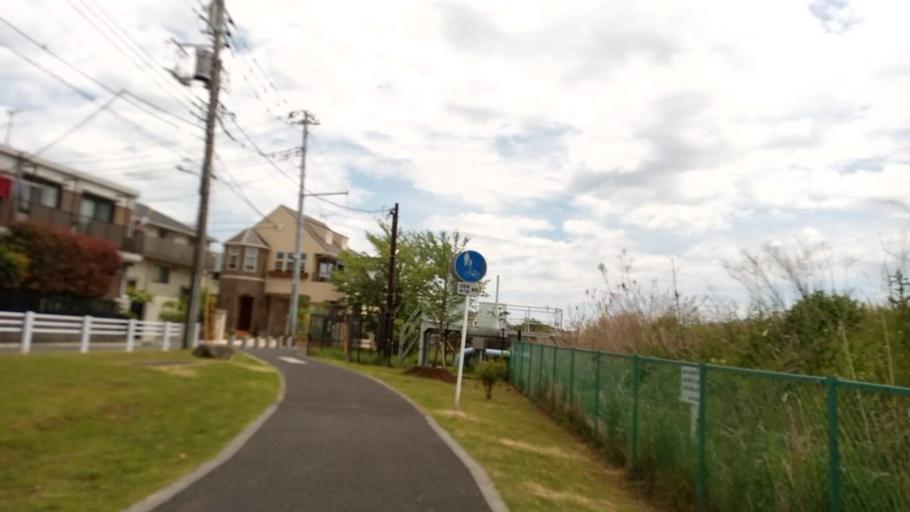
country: JP
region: Chiba
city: Abiko
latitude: 35.8637
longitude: 140.0197
